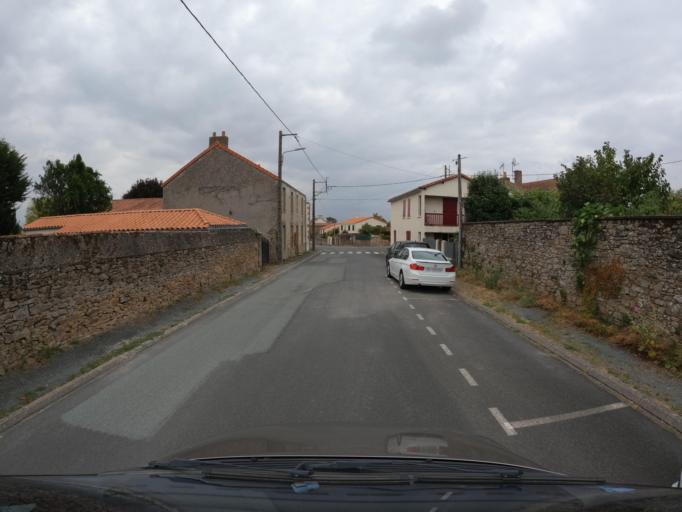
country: FR
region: Pays de la Loire
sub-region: Departement de la Vendee
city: Tiffauges
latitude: 47.0105
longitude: -1.1101
